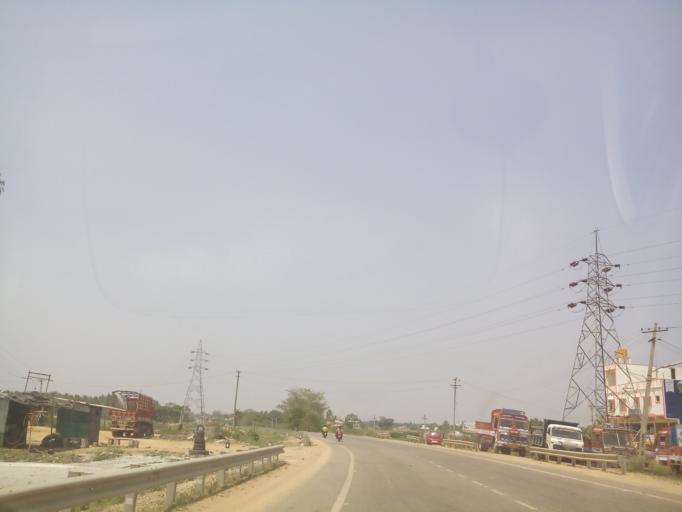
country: IN
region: Karnataka
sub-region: Hassan
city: Hassan
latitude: 12.9915
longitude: 76.0869
